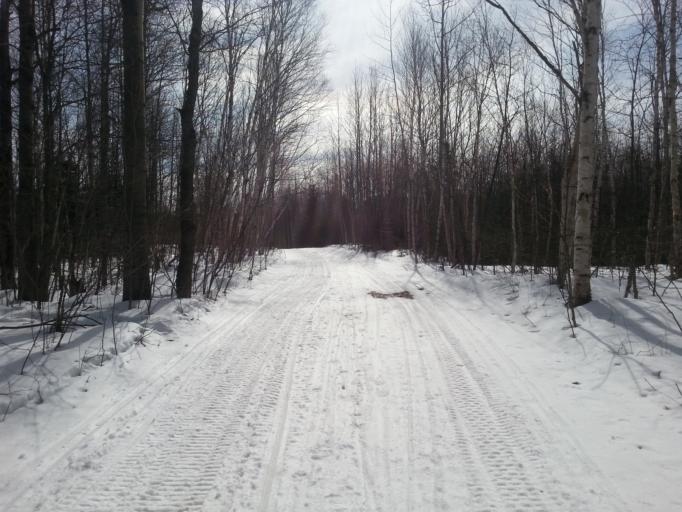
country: CA
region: Ontario
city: Greater Sudbury
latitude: 46.3454
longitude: -80.9015
